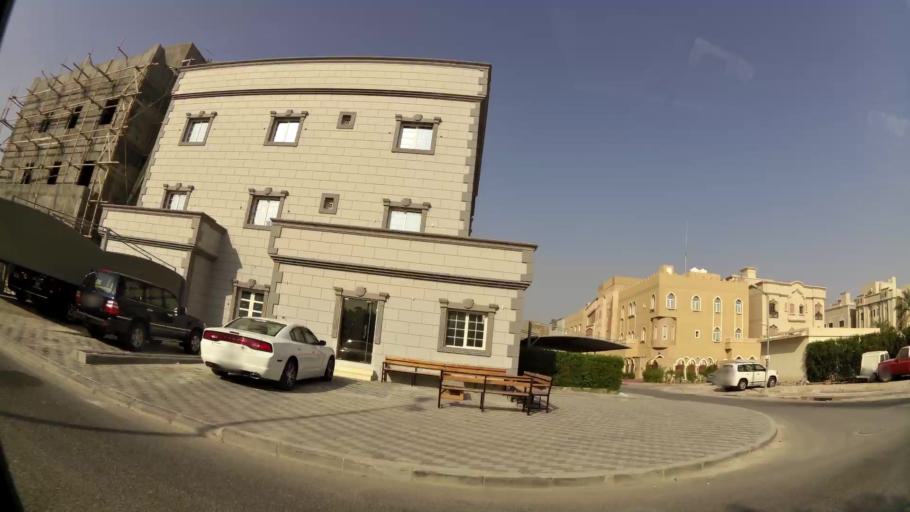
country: KW
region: Al Asimah
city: Ar Rabiyah
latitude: 29.3054
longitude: 47.7993
